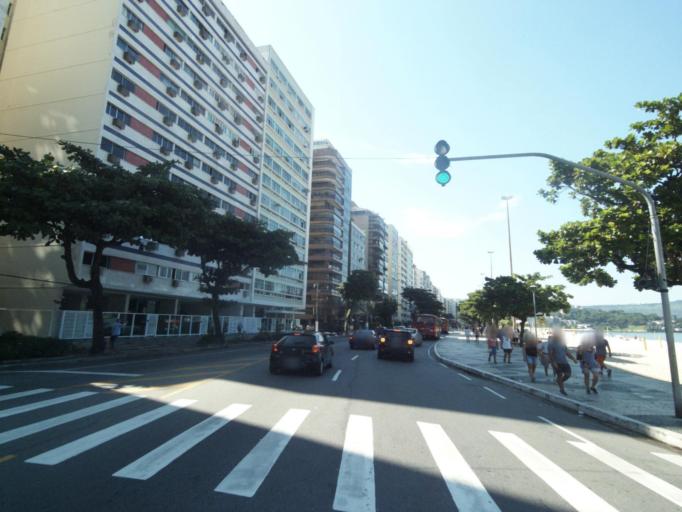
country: BR
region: Rio de Janeiro
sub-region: Niteroi
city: Niteroi
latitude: -22.9048
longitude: -43.1151
